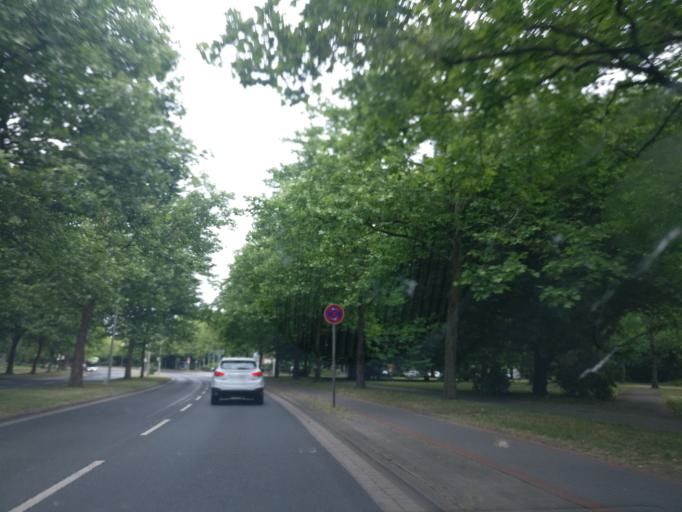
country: DE
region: Lower Saxony
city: Hannover
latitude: 52.3908
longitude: 9.8054
